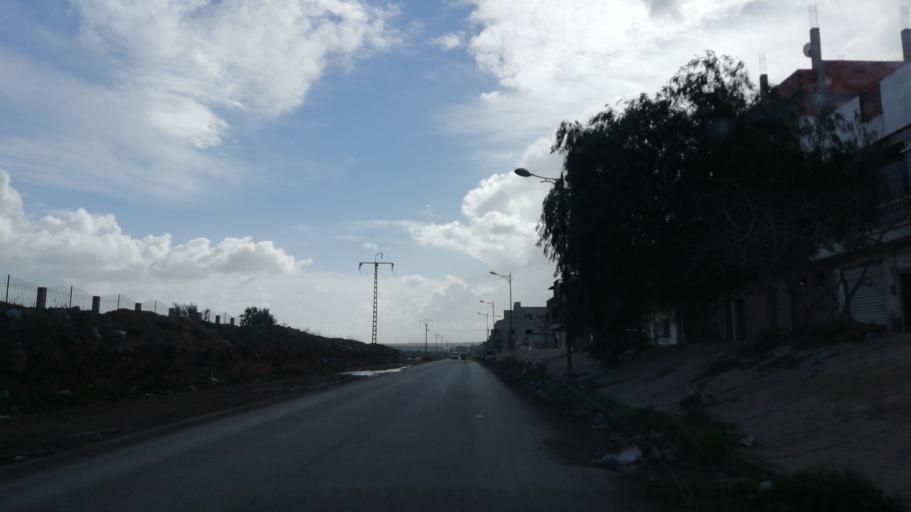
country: DZ
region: Oran
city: Sidi ech Chahmi
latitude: 35.6477
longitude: -0.5616
